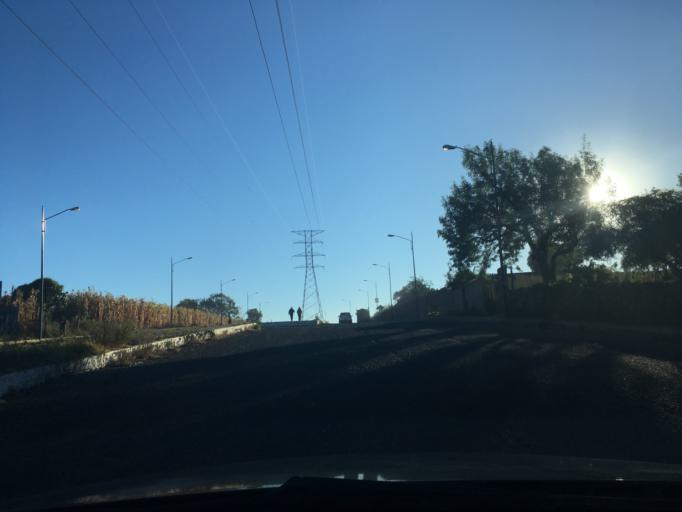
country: MX
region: Michoacan
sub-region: Morelia
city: Montana Monarca (Punta Altozano)
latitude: 19.6561
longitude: -101.1848
